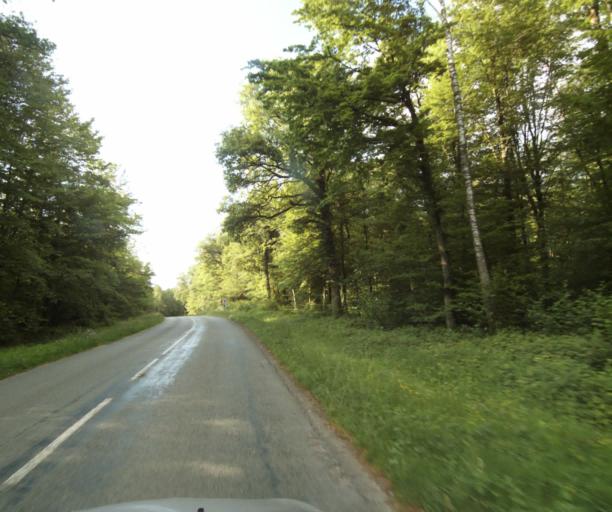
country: FR
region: Champagne-Ardenne
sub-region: Departement des Ardennes
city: Warcq
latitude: 49.8186
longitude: 4.6995
